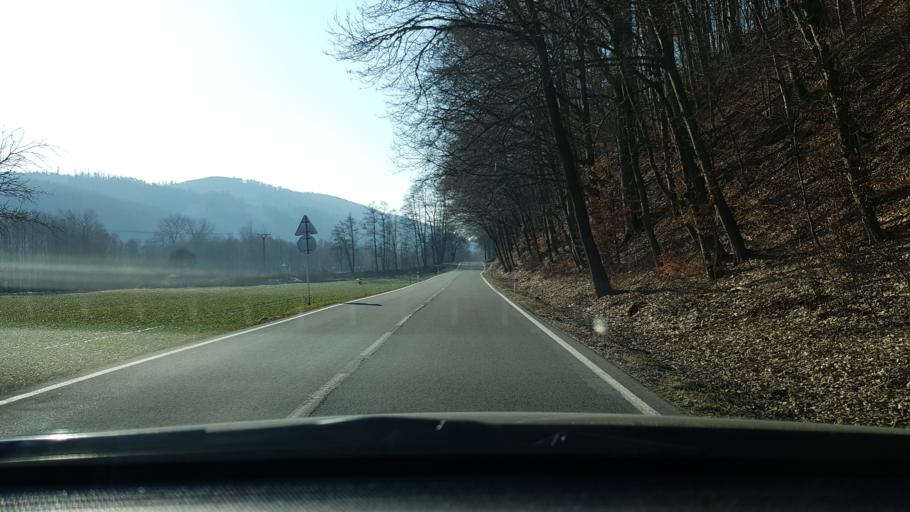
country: CZ
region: Olomoucky
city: Dolni Bohdikov
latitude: 50.0083
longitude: 16.8947
